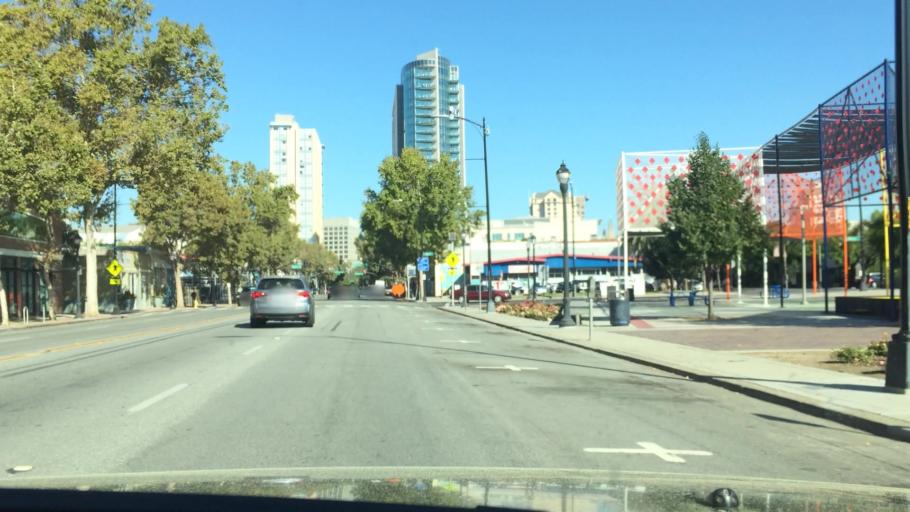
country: US
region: California
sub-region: Santa Clara County
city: San Jose
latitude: 37.3280
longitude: -121.8848
